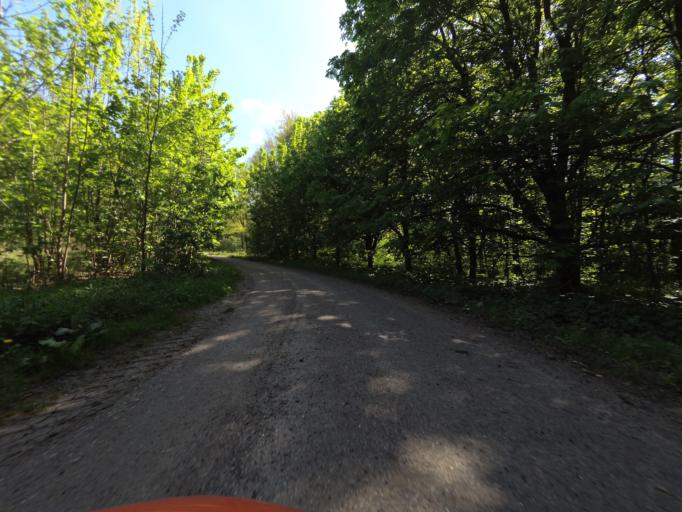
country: NL
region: Gelderland
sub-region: Gemeente Harderwijk
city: Harderwijk
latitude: 52.4007
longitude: 5.6254
